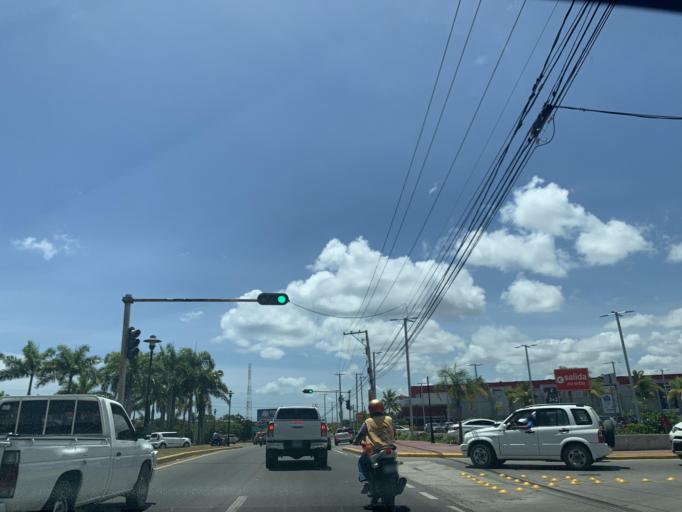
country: DO
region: Puerto Plata
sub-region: Puerto Plata
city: Puerto Plata
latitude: 19.7827
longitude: -70.6742
